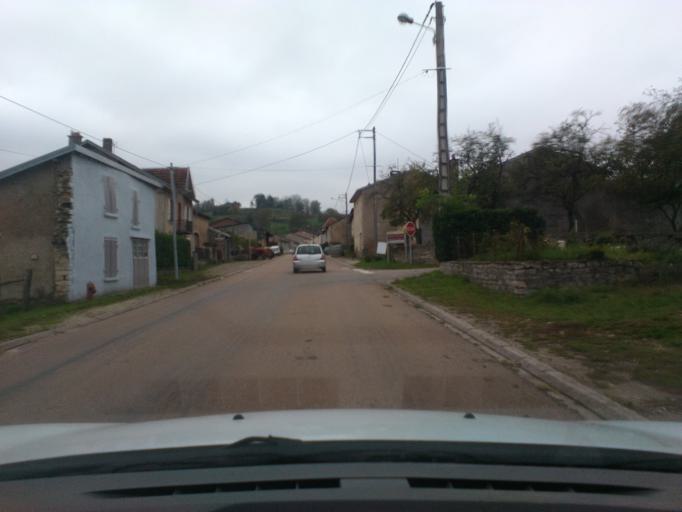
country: FR
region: Lorraine
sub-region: Departement des Vosges
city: Vincey
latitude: 48.3024
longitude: 6.2727
